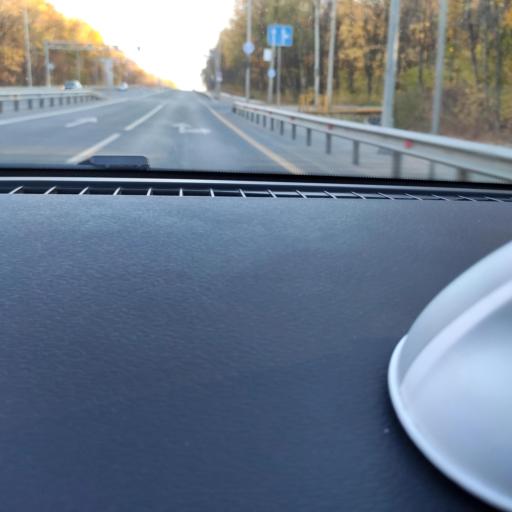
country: RU
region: Samara
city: Petra-Dubrava
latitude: 53.2874
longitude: 50.2496
